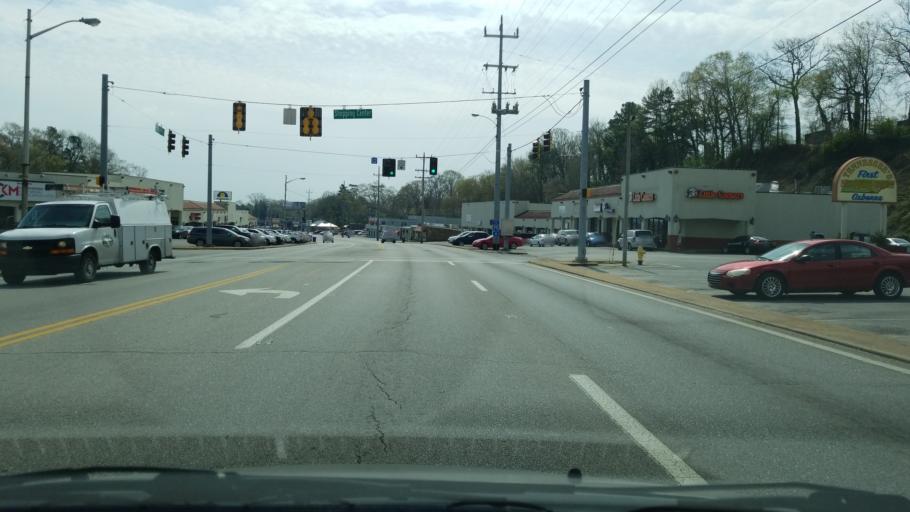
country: US
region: Tennessee
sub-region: Hamilton County
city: East Ridge
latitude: 35.0005
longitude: -85.2577
